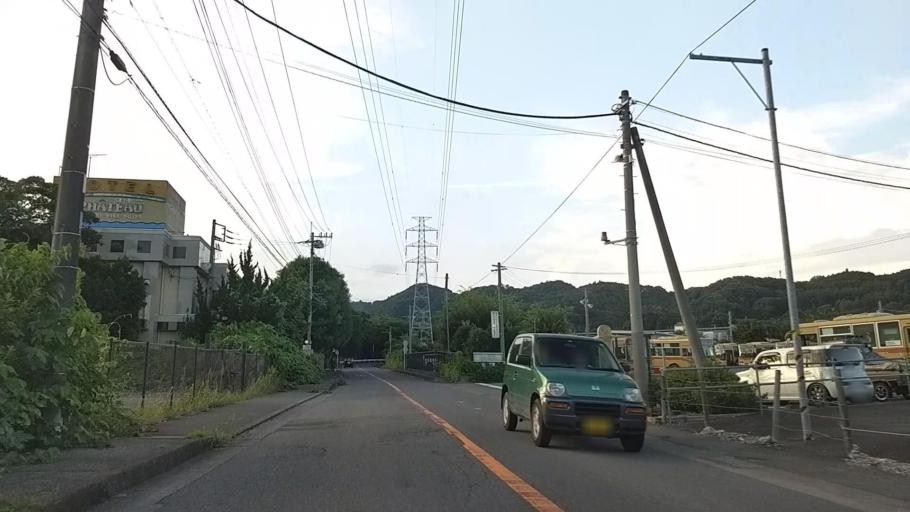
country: JP
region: Tokyo
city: Hachioji
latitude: 35.5904
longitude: 139.2835
